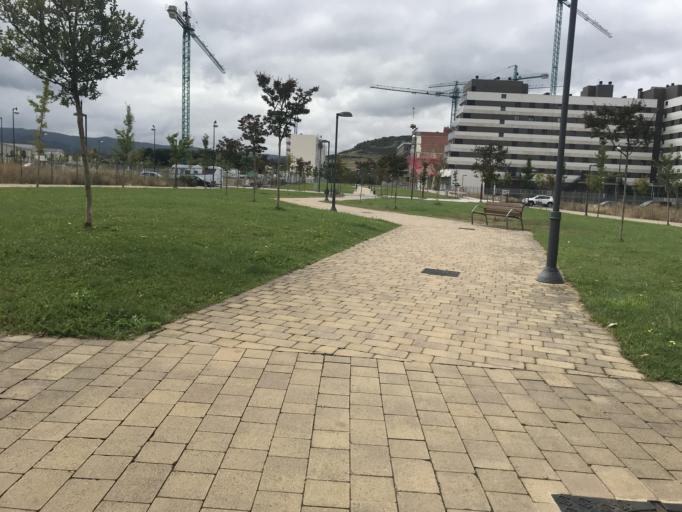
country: ES
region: Basque Country
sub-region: Provincia de Alava
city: Gasteiz / Vitoria
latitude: 42.8328
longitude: -2.6586
